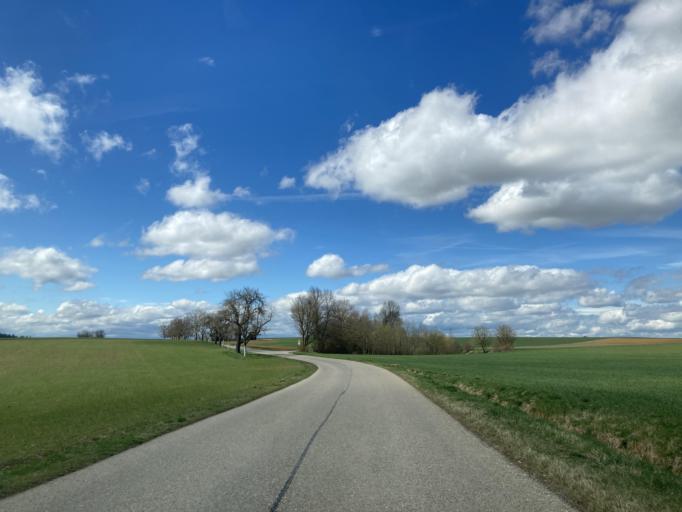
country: DE
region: Baden-Wuerttemberg
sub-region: Tuebingen Region
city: Hirrlingen
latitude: 48.4569
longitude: 8.8415
